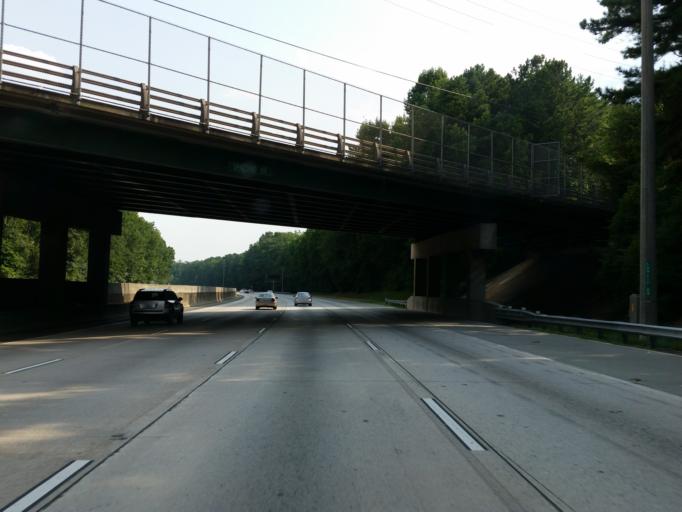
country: US
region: Georgia
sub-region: DeKalb County
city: Dunwoody
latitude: 33.9572
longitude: -84.3561
